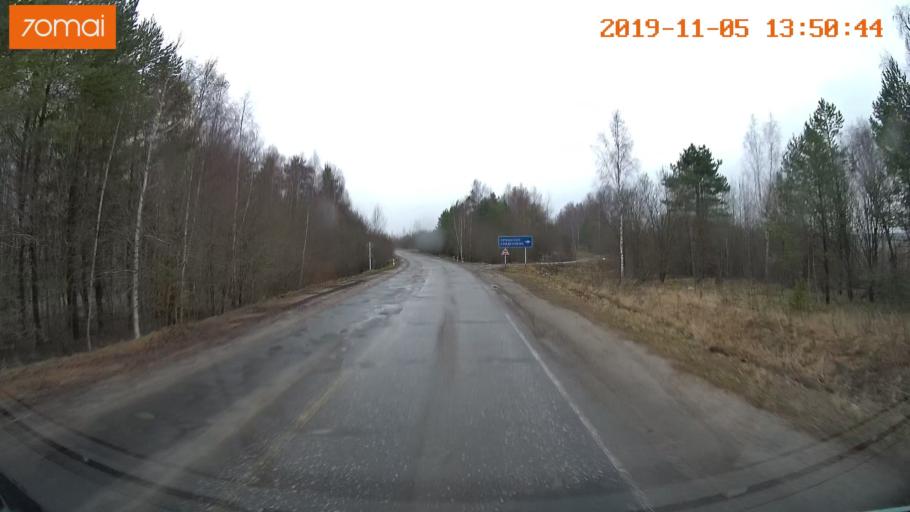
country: RU
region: Ivanovo
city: Kaminskiy
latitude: 57.0215
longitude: 41.4065
